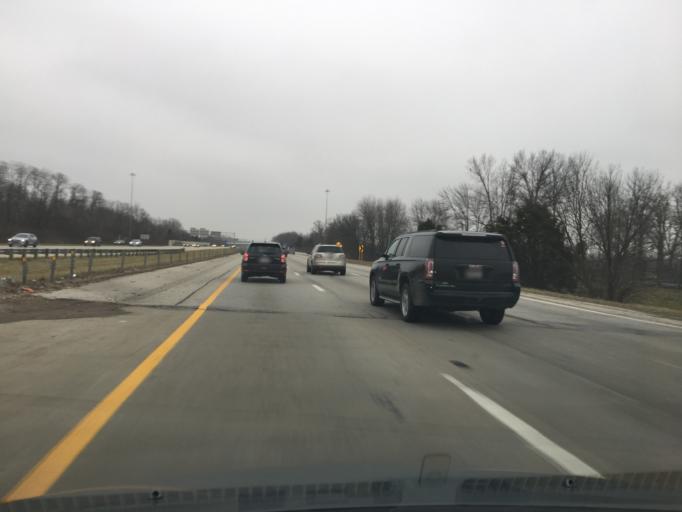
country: US
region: Ohio
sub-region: Hamilton County
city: Highpoint
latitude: 39.2696
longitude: -84.3494
